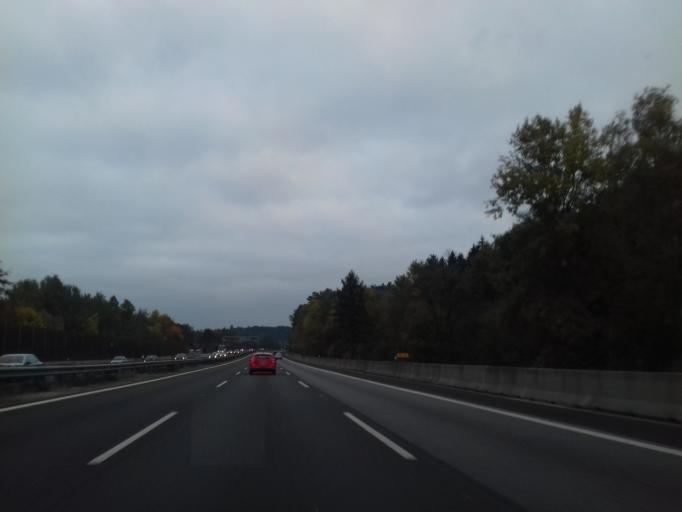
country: CZ
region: Central Bohemia
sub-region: Okres Praha-Vychod
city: Strancice
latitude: 49.9339
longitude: 14.6894
